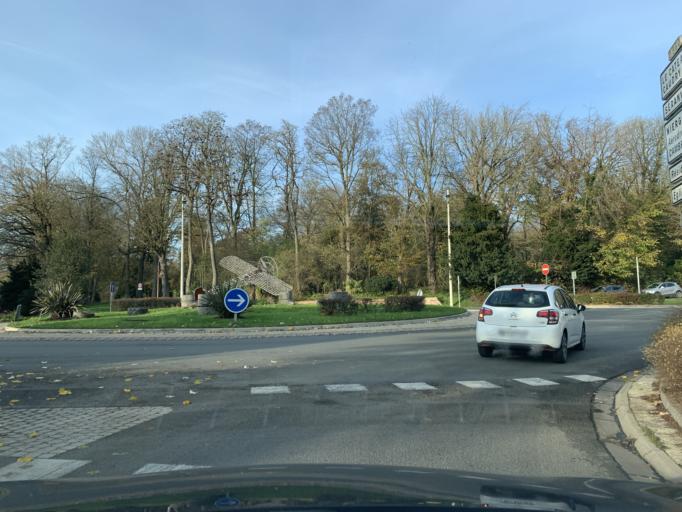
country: FR
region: Nord-Pas-de-Calais
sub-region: Departement du Nord
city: Cambrai
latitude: 50.1676
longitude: 3.2411
